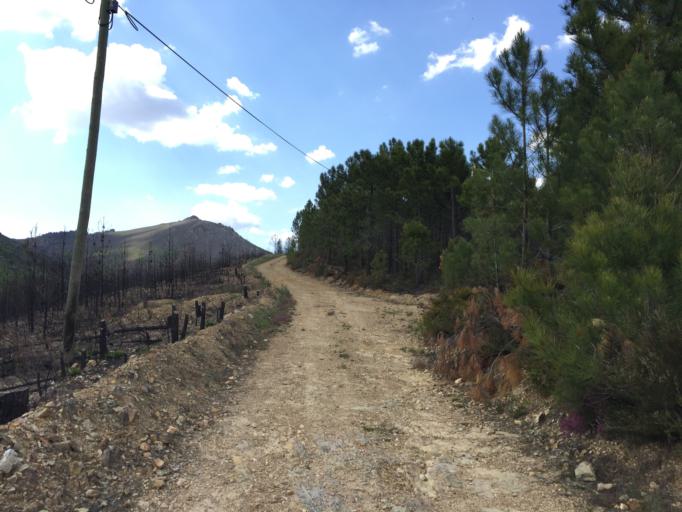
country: PT
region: Coimbra
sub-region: Pampilhosa da Serra
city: Pampilhosa da Serra
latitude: 40.1032
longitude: -7.8662
